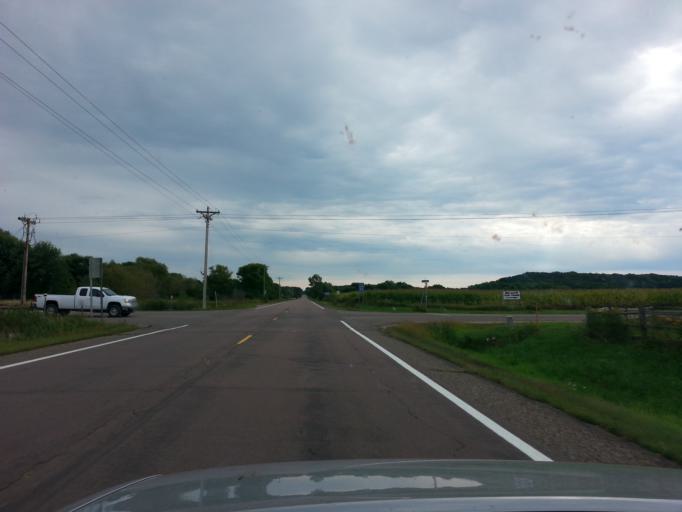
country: US
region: Minnesota
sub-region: Dakota County
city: Farmington
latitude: 44.6303
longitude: -93.0561
